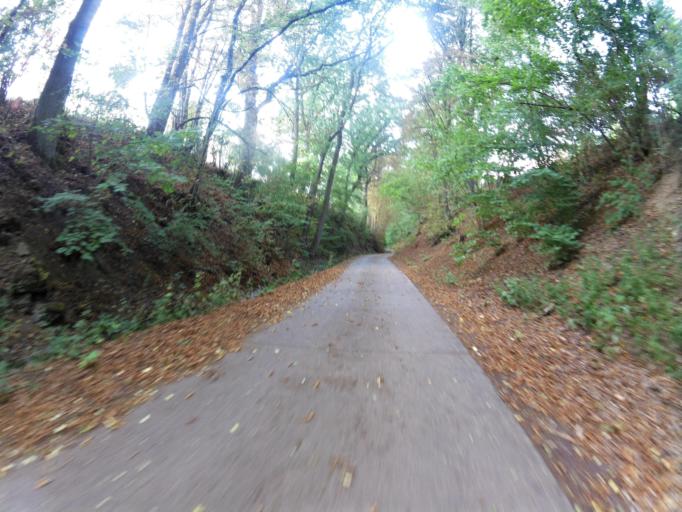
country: DE
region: Bavaria
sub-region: Regierungsbezirk Unterfranken
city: Ochsenfurt
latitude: 49.6524
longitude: 10.0593
